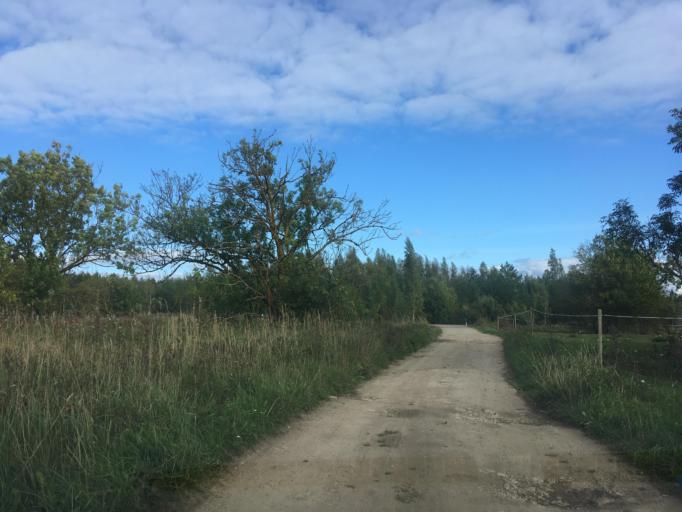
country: EE
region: Harju
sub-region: Maardu linn
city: Maardu
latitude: 59.4532
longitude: 25.0482
